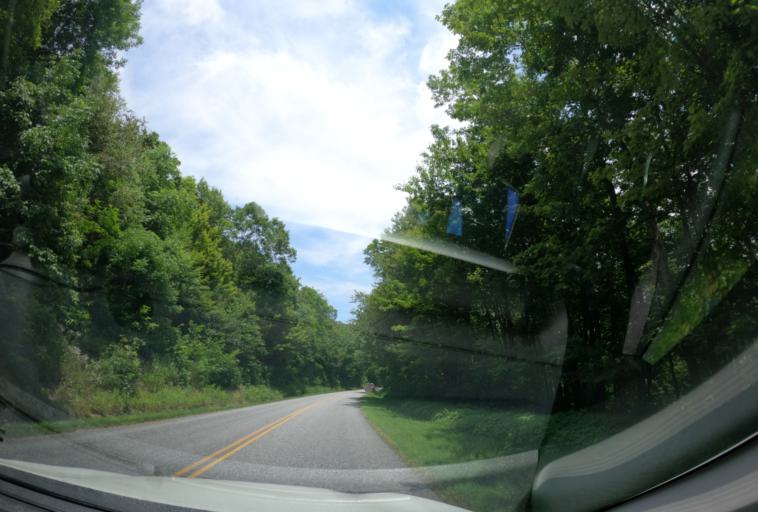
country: US
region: North Carolina
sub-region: Haywood County
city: Canton
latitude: 35.4294
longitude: -82.7390
